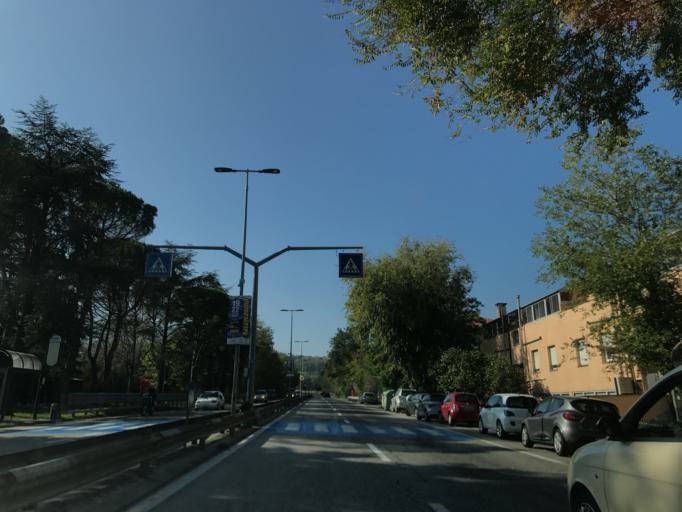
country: SM
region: Serravalle
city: Serravalle
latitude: 43.9669
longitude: 12.4745
